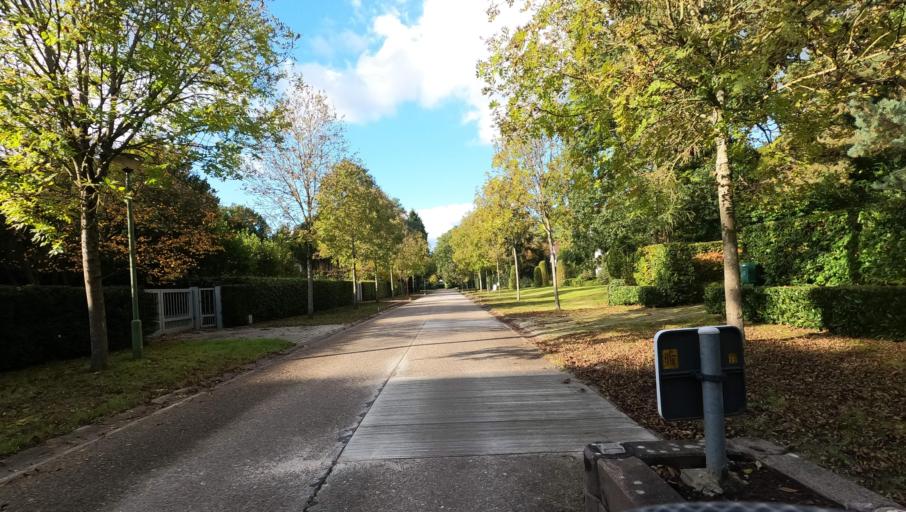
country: BE
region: Flanders
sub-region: Provincie Antwerpen
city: Schilde
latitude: 51.2395
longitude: 4.5724
